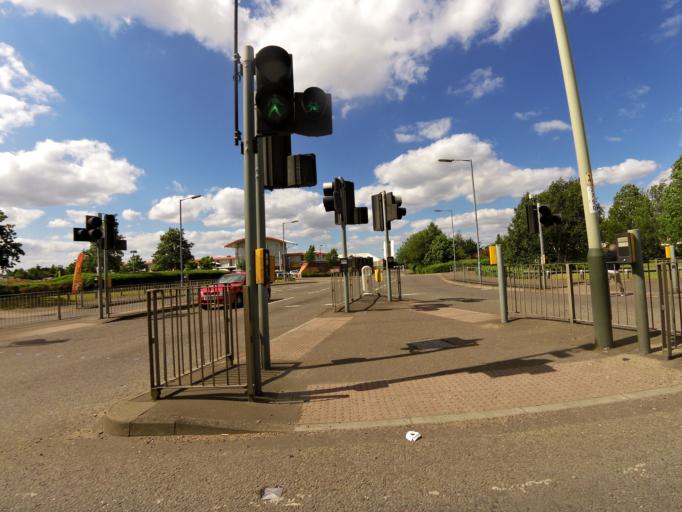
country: GB
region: England
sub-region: Norfolk
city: Norwich
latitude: 52.6551
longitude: 1.2722
